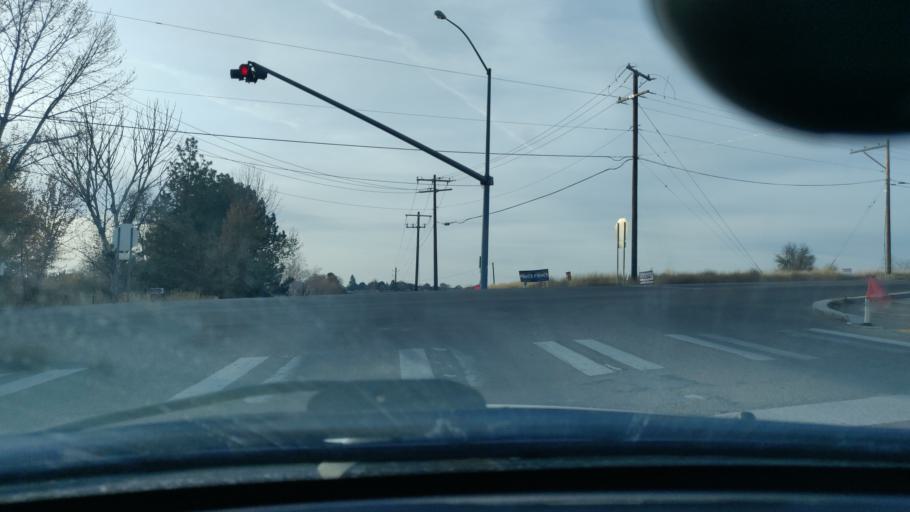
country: US
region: Idaho
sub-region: Ada County
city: Eagle
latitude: 43.6923
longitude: -116.3137
